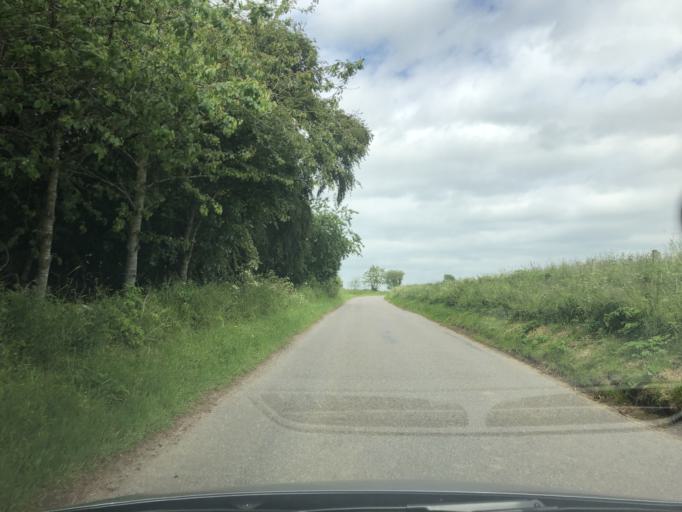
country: GB
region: Scotland
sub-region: Angus
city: Forfar
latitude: 56.7215
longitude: -2.9282
